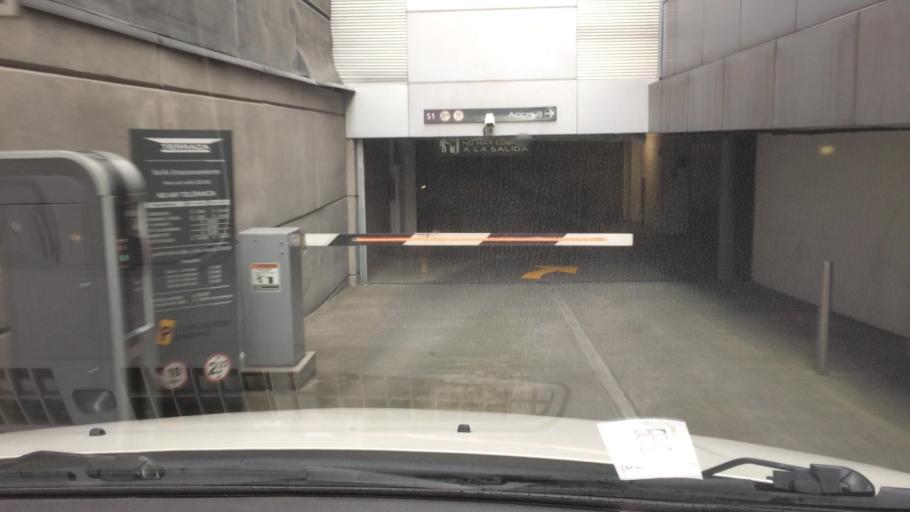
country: MX
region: Mexico City
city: Magdalena Contreras
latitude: 19.3069
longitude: -99.2097
